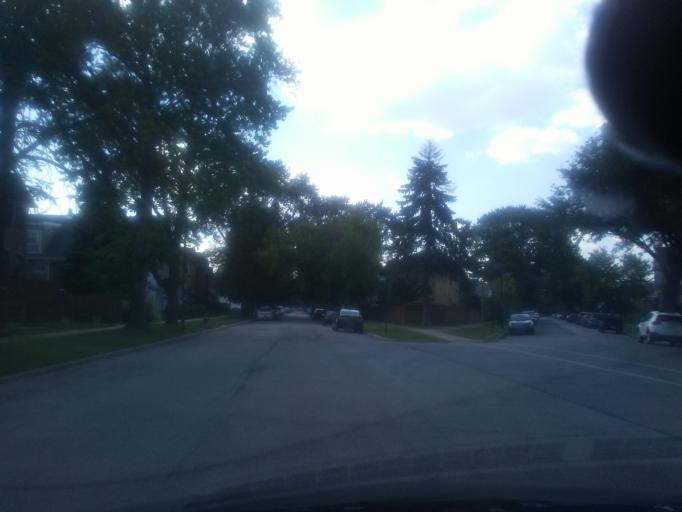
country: US
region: Illinois
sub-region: Cook County
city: Harwood Heights
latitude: 41.9696
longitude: -87.7685
